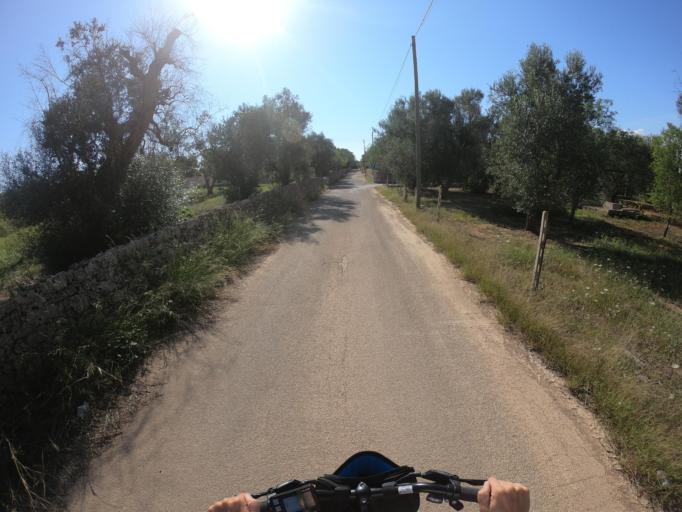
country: IT
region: Apulia
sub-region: Provincia di Lecce
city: Galatone
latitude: 40.1508
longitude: 18.0423
